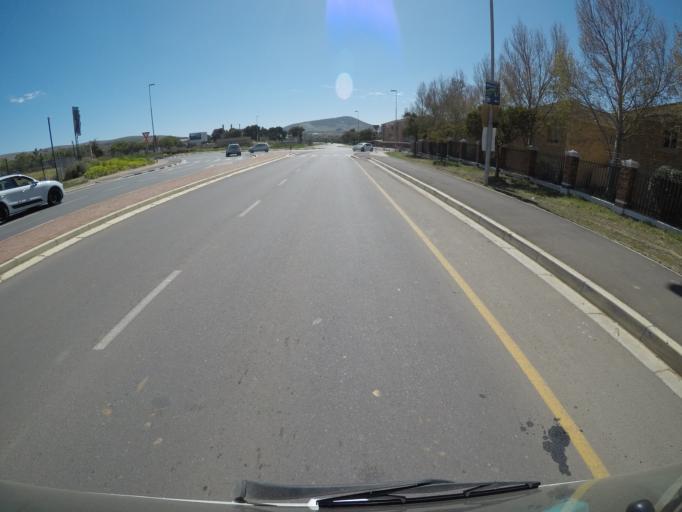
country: ZA
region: Western Cape
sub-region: City of Cape Town
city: Kraaifontein
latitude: -33.8190
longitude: 18.6350
